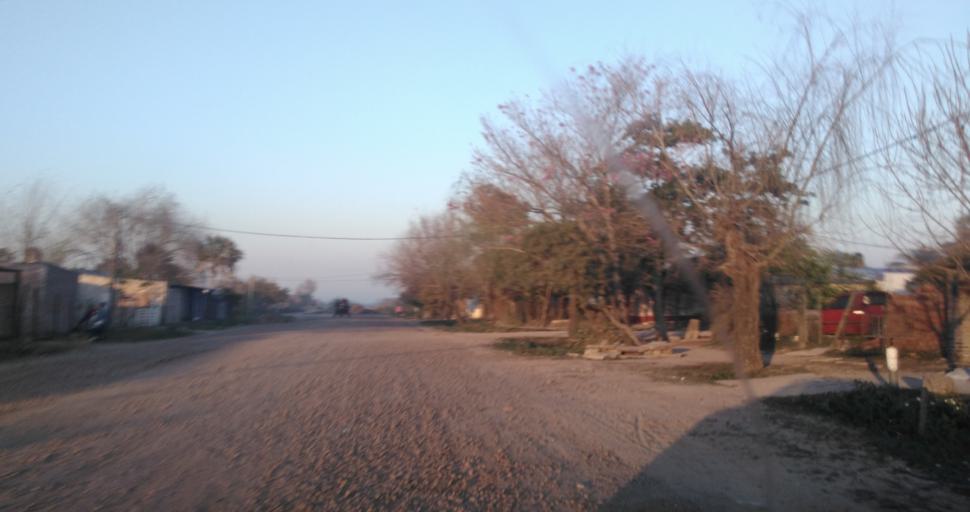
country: AR
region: Chaco
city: Resistencia
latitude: -27.4884
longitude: -58.9997
